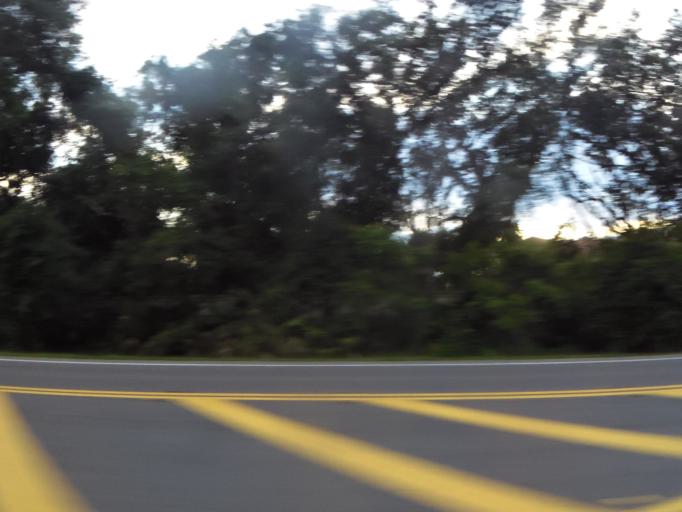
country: US
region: Florida
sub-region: Nassau County
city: Fernandina Beach
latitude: 30.5991
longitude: -81.4482
